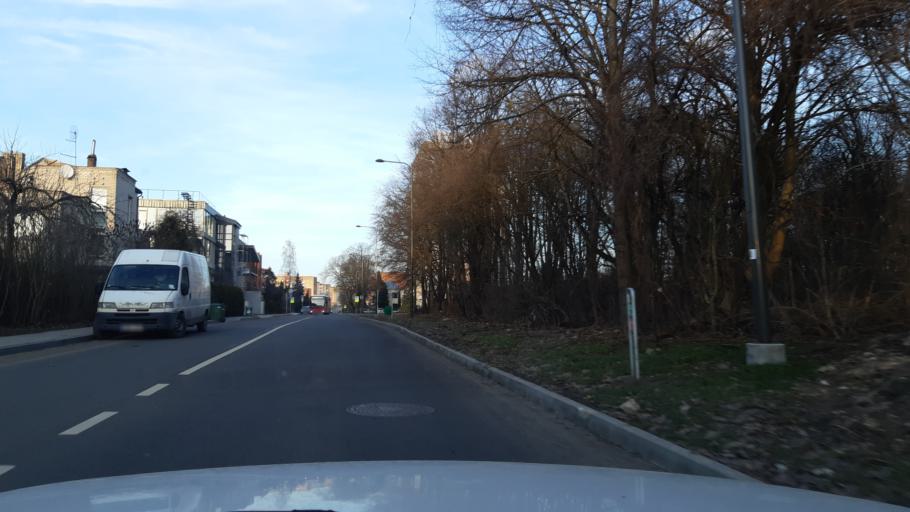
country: LT
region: Kauno apskritis
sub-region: Kaunas
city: Aleksotas
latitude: 54.8867
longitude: 23.9386
